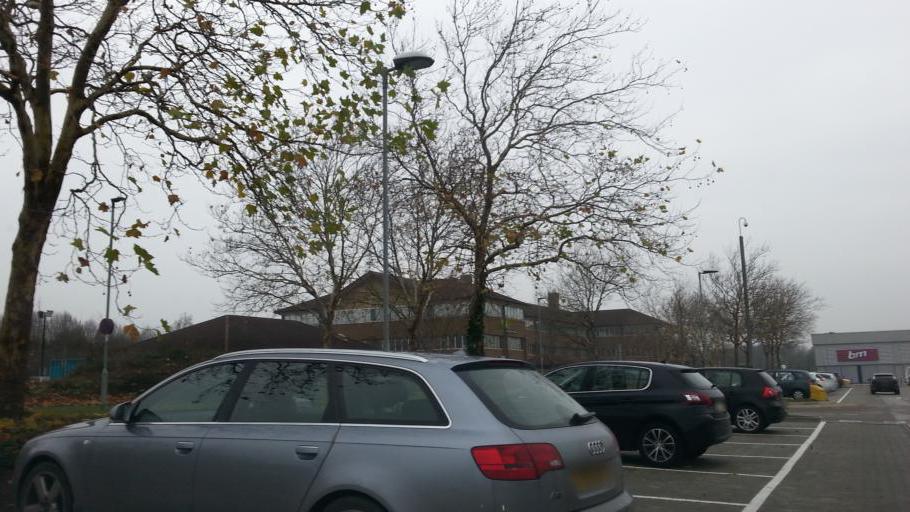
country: GB
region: England
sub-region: Cambridgeshire
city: Yaxley
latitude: 52.5429
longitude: -0.3038
